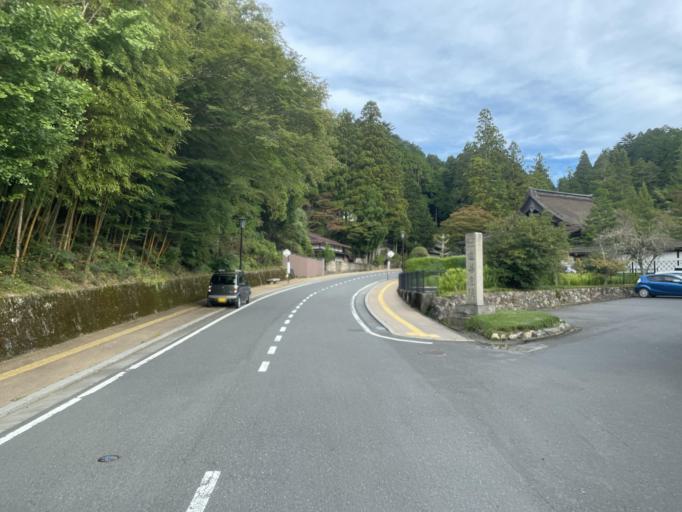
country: JP
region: Wakayama
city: Koya
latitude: 34.2175
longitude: 135.5815
